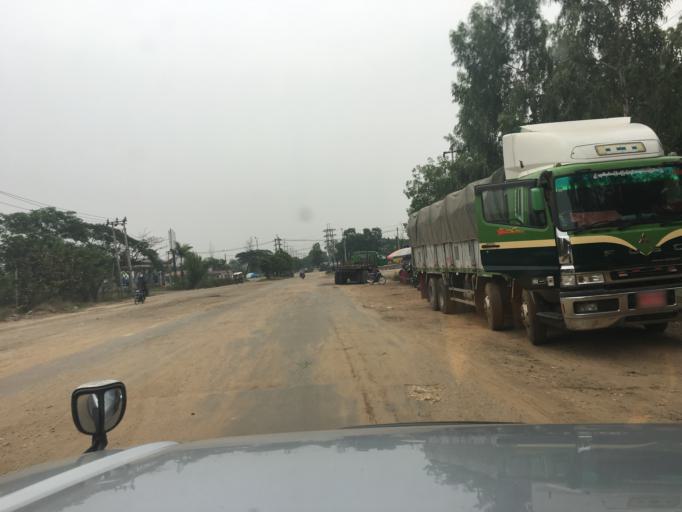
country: MM
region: Yangon
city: Syriam
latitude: 16.9470
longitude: 96.2817
